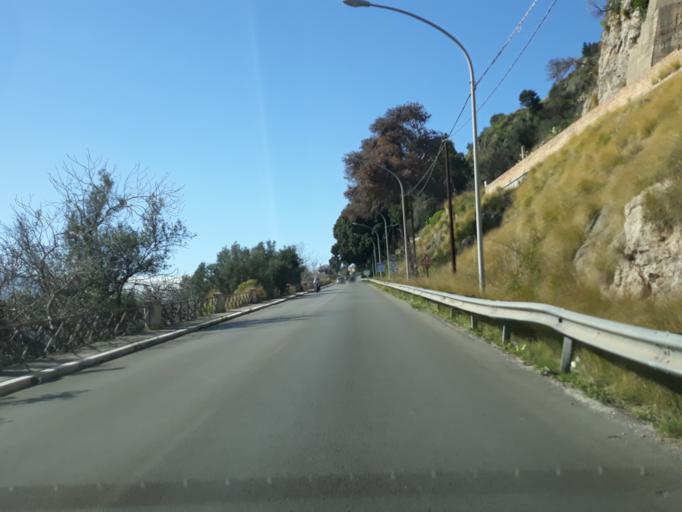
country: IT
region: Sicily
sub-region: Palermo
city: Monreale
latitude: 38.0928
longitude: 13.3044
